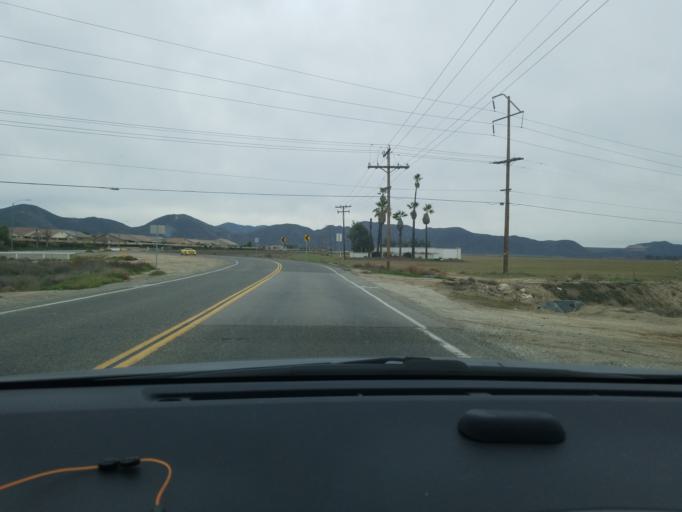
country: US
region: California
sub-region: Riverside County
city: Green Acres
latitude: 33.7249
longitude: -117.0327
